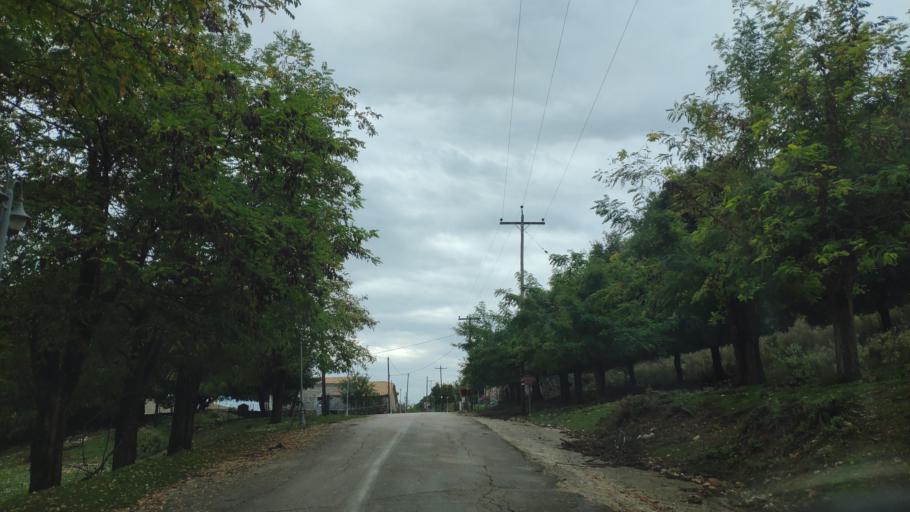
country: GR
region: Epirus
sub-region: Nomos Prevezis
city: Kanalaki
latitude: 39.3604
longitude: 20.6408
